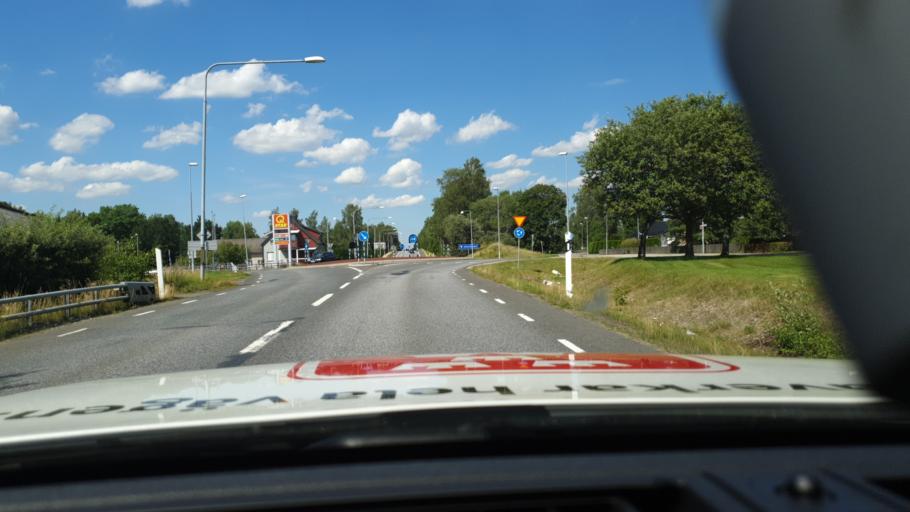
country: SE
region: Joenkoeping
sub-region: Vaggeryds Kommun
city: Vaggeryd
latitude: 57.5118
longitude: 14.2796
